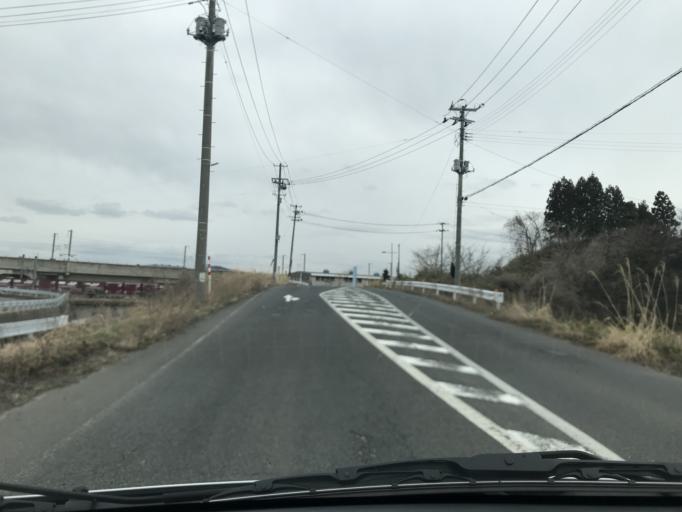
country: JP
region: Iwate
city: Kitakami
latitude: 39.2664
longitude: 141.1131
